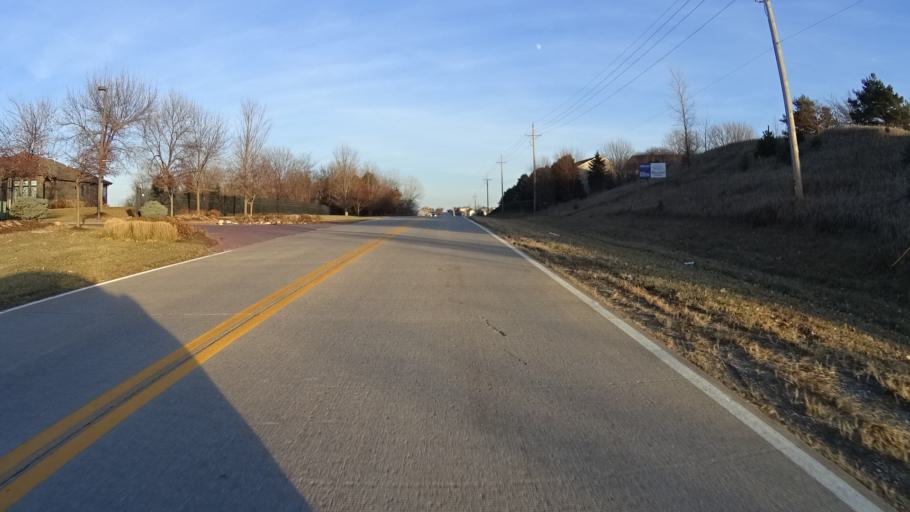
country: US
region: Nebraska
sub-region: Sarpy County
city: Papillion
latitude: 41.1326
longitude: -96.0728
